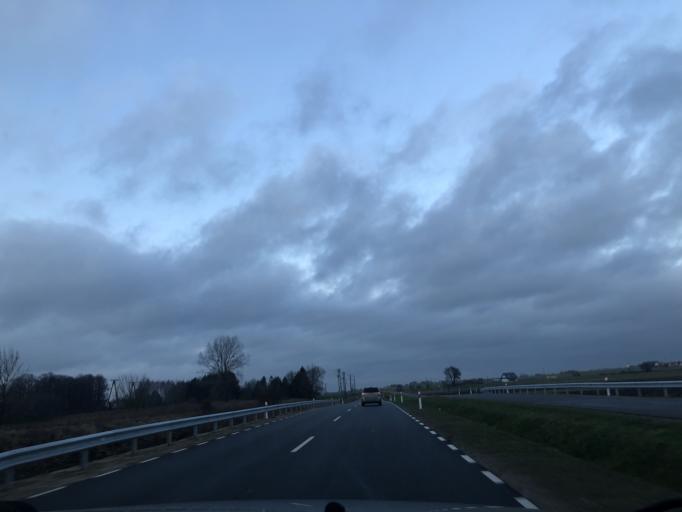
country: PL
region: Podlasie
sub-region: Lomza
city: Lomza
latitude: 53.1334
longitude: 22.0496
